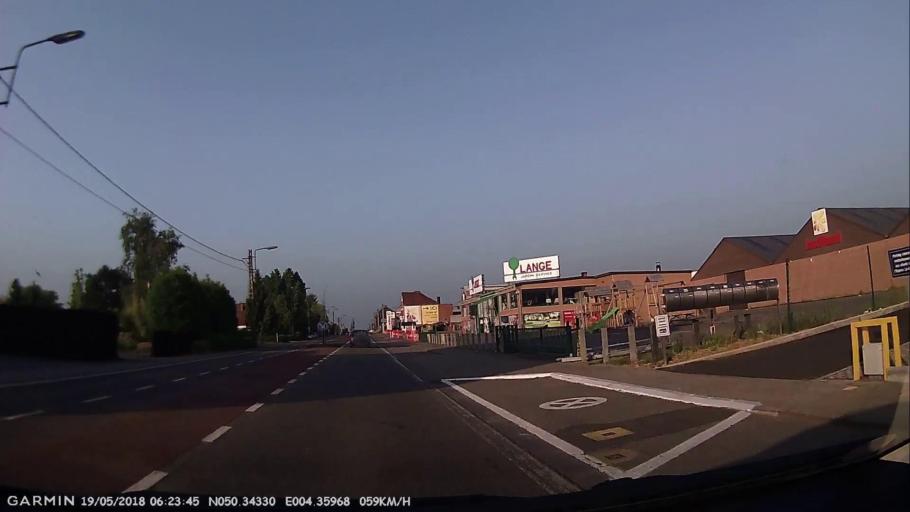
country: BE
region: Wallonia
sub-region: Province du Hainaut
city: Thuin
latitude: 50.3431
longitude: 4.3595
